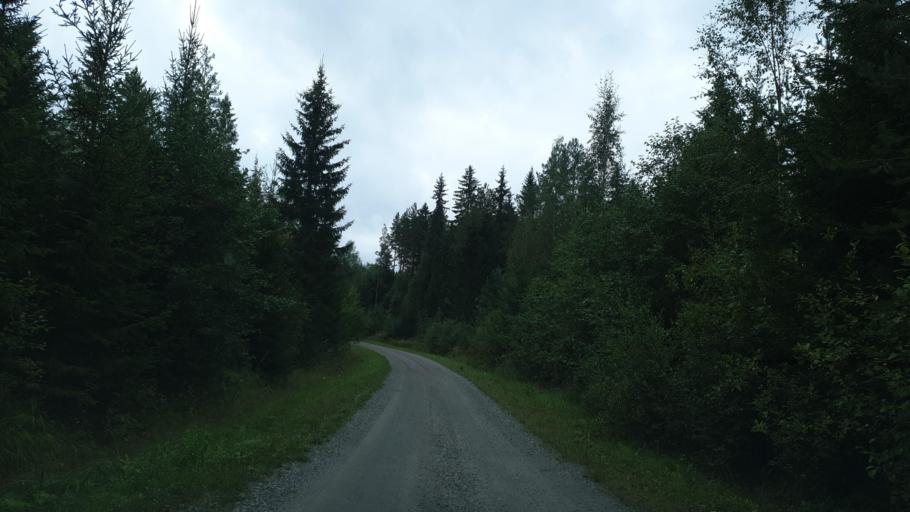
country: FI
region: Northern Savo
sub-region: Kuopio
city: Nilsiae
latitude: 63.2438
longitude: 28.2552
